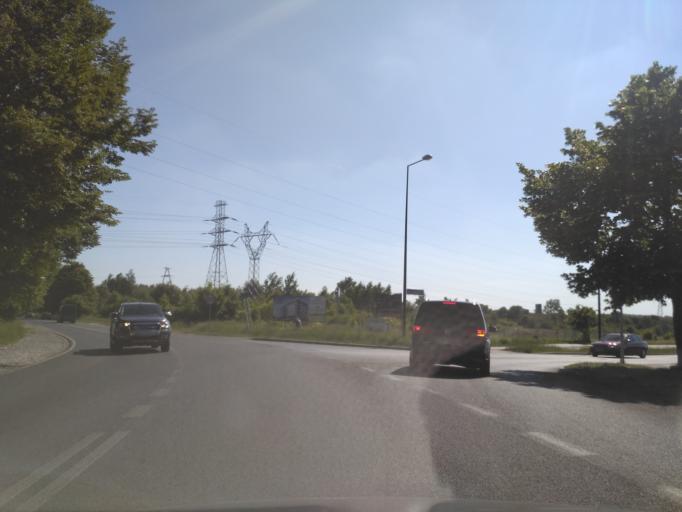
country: PL
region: Lublin Voivodeship
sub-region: Powiat lubelski
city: Lublin
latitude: 51.1953
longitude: 22.5474
